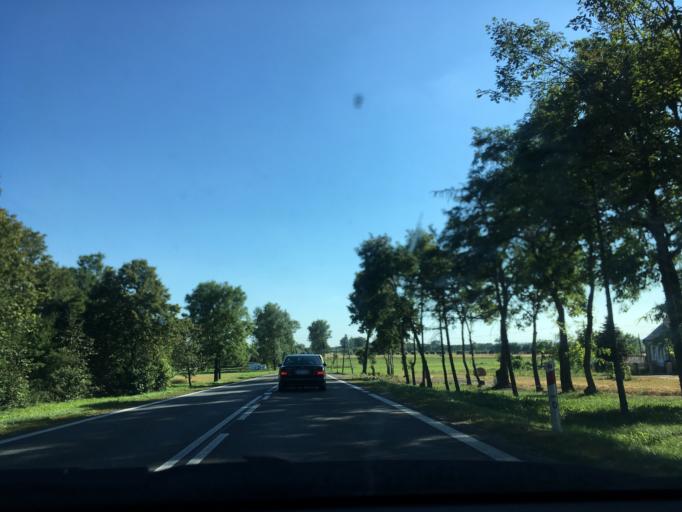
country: PL
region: Podlasie
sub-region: Powiat sokolski
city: Suchowola
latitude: 53.5217
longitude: 23.1060
